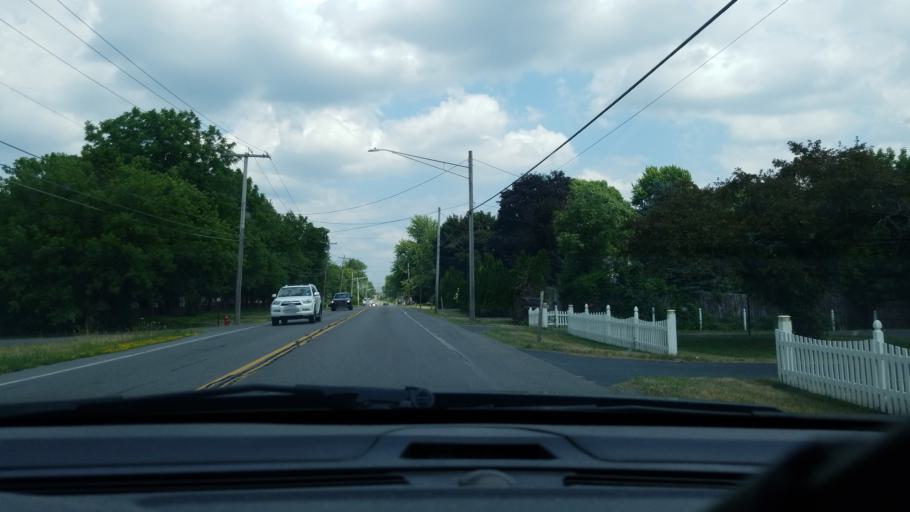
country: US
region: New York
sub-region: Onondaga County
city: Liverpool
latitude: 43.1502
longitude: -76.2137
